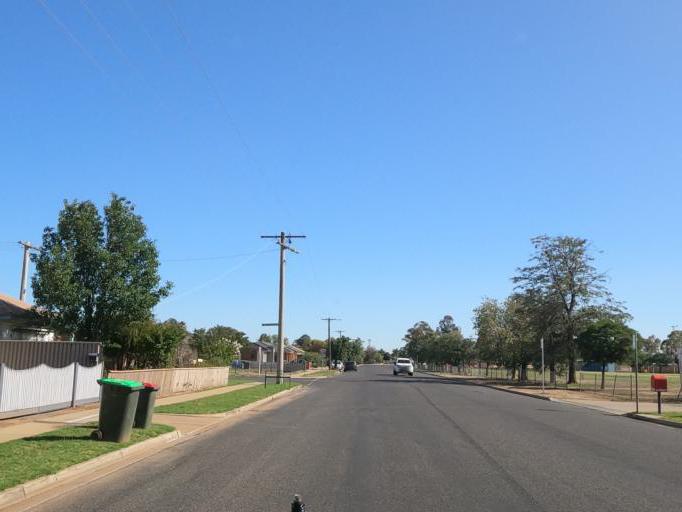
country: AU
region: Victoria
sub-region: Moira
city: Yarrawonga
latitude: -36.0214
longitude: 146.0054
